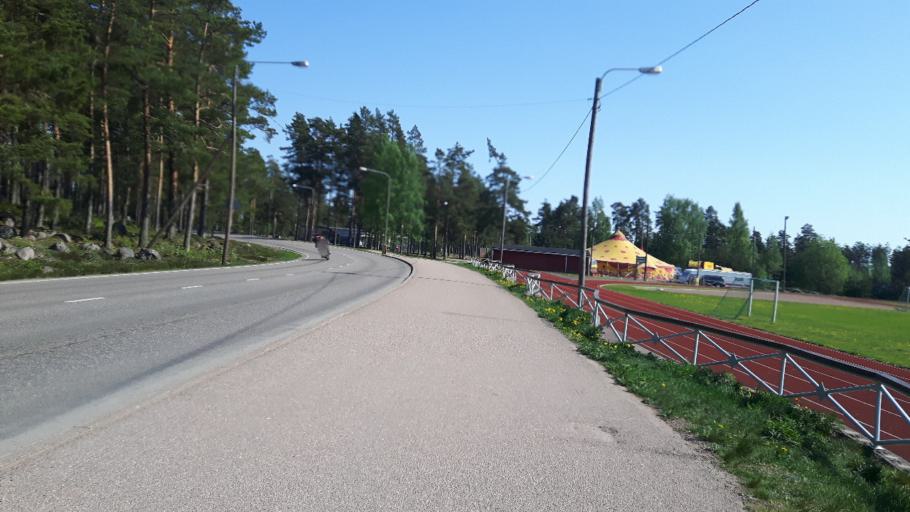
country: FI
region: Kymenlaakso
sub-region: Kotka-Hamina
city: Broby
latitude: 60.4884
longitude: 26.7476
